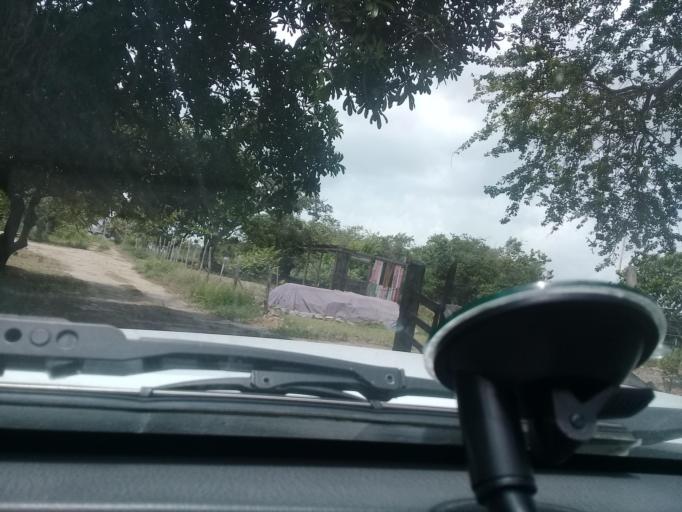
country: MX
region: Veracruz
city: Anahuac
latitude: 22.2226
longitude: -97.8264
